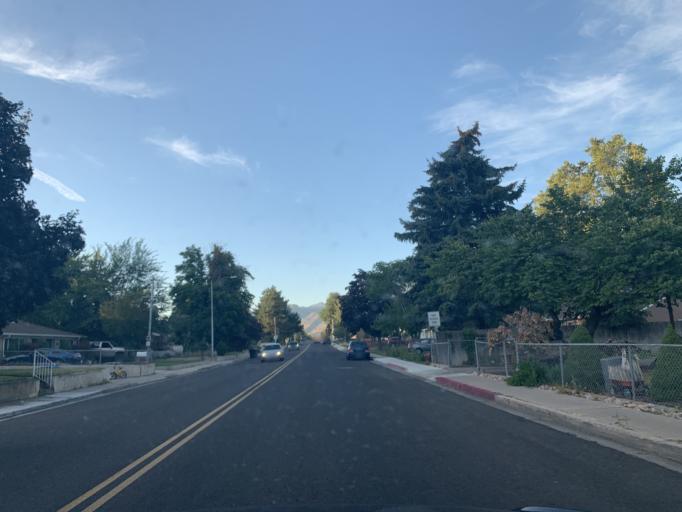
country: US
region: Utah
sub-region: Utah County
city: Orem
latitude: 40.2662
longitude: -111.6950
